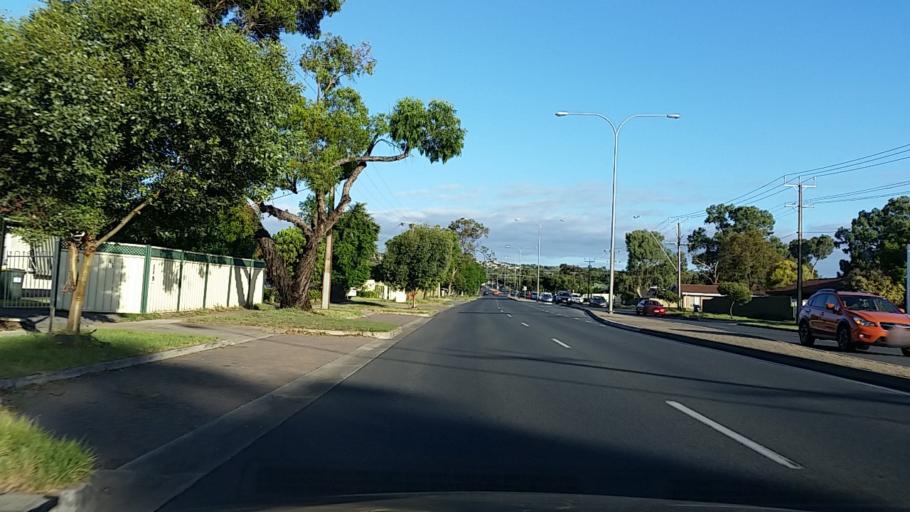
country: AU
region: South Australia
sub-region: Salisbury
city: Salisbury
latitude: -34.7940
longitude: 138.6509
